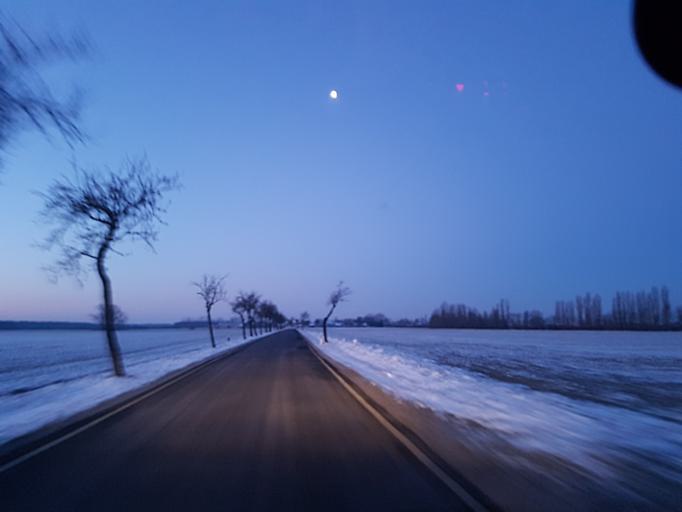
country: DE
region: Brandenburg
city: Falkenberg
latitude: 51.5096
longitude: 13.2939
